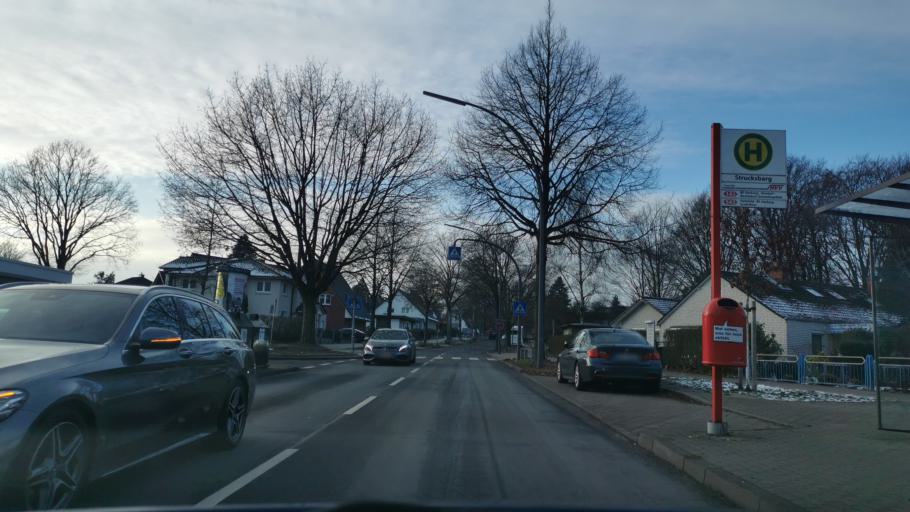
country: DE
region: Hamburg
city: Harburg
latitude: 53.4499
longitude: 9.9373
